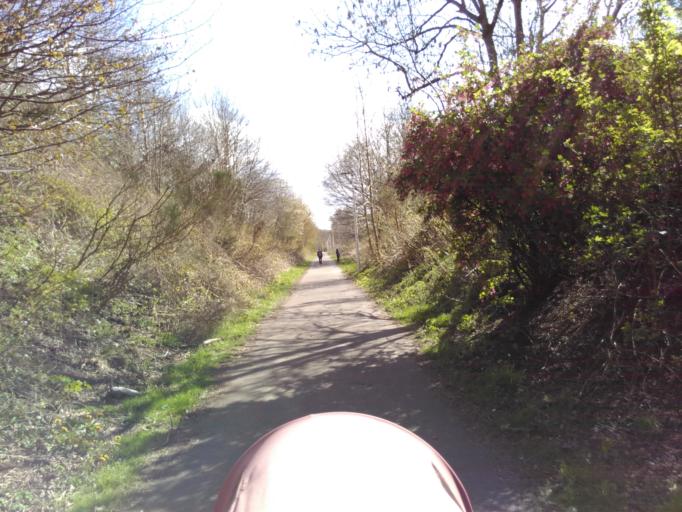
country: GB
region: Scotland
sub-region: Midlothian
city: Loanhead
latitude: 55.8751
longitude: -3.1501
